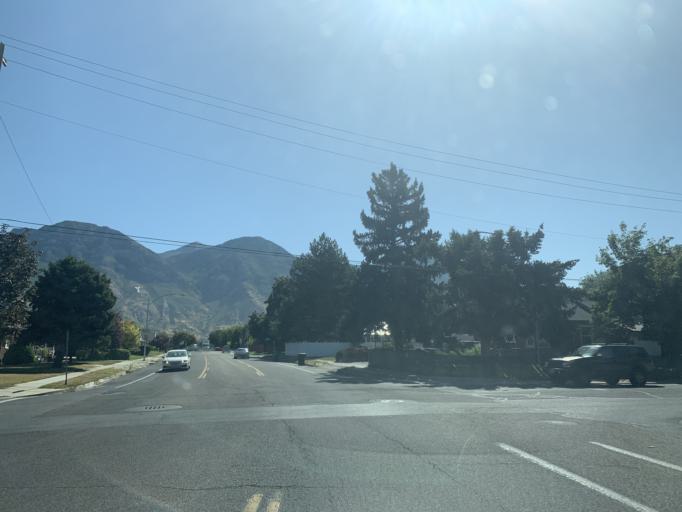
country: US
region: Utah
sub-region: Utah County
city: Provo
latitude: 40.2444
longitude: -111.6731
